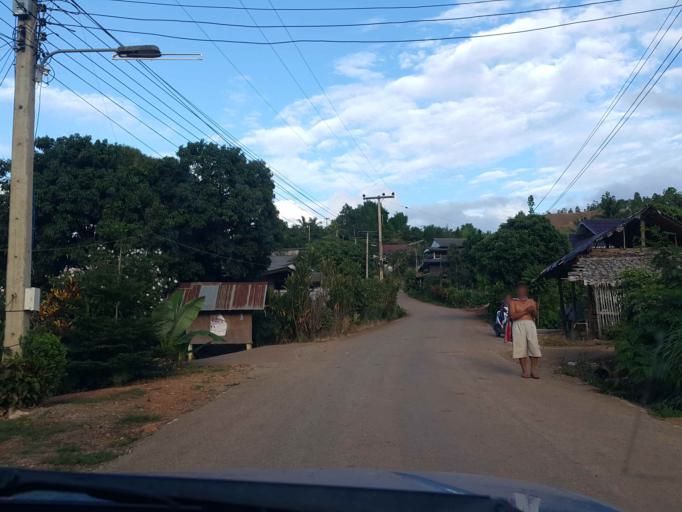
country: TH
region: Chiang Mai
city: Mae Chaem
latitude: 18.5145
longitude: 98.4007
